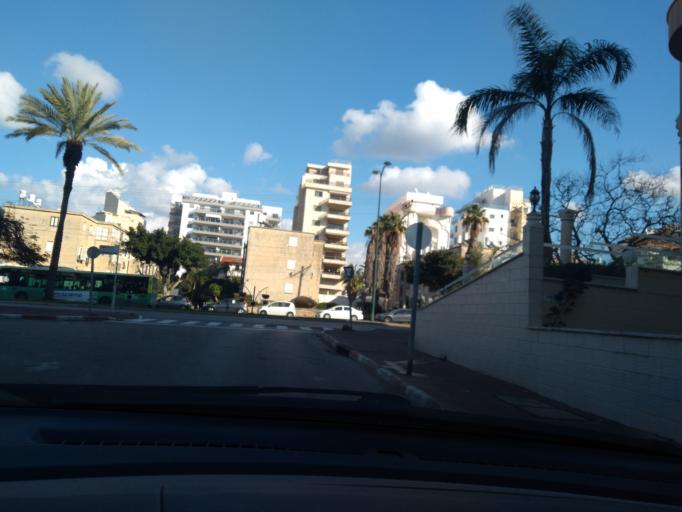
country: IL
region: Central District
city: Netanya
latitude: 32.3373
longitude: 34.8592
